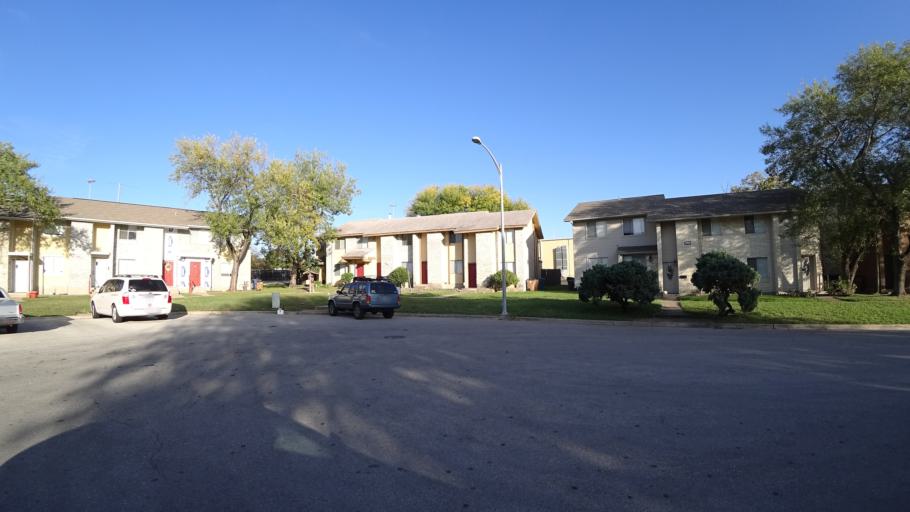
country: US
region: Texas
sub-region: Williamson County
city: Jollyville
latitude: 30.3746
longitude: -97.7334
